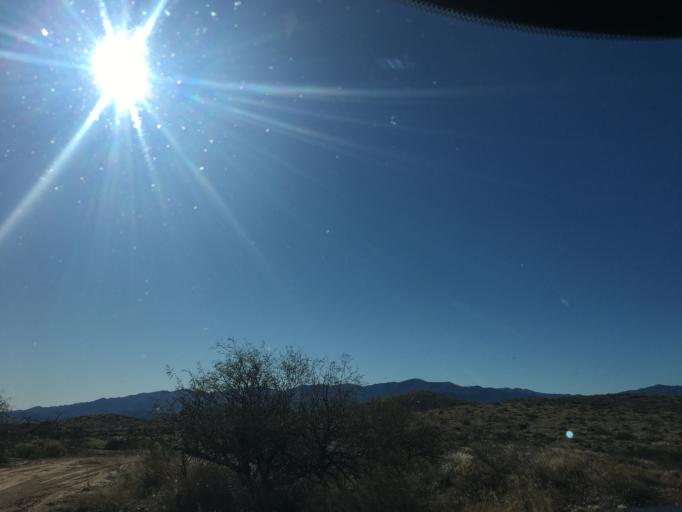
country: US
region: Arizona
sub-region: Yavapai County
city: Cordes Lakes
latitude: 34.2875
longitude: -112.1249
